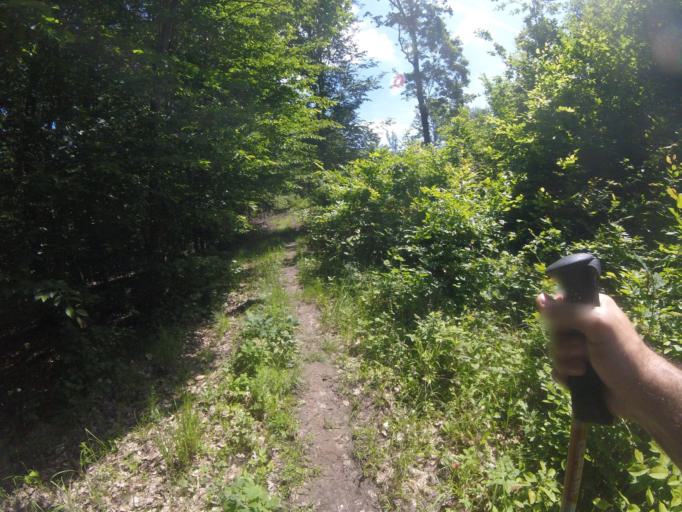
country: HU
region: Nograd
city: Batonyterenye
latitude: 47.9283
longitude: 19.8074
